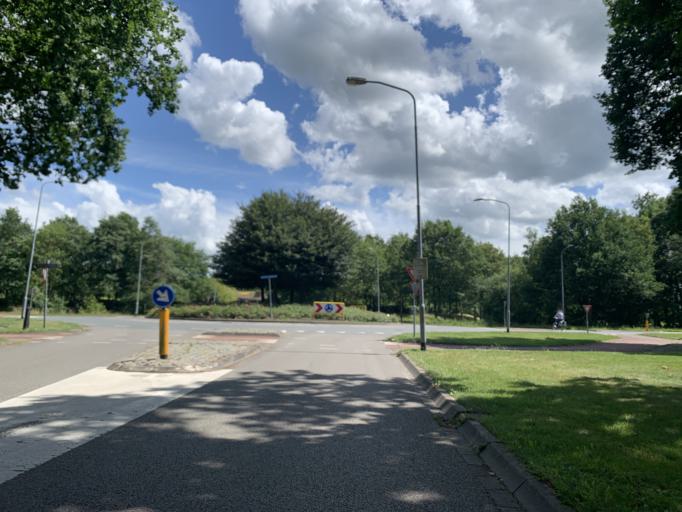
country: NL
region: Groningen
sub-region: Gemeente Haren
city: Haren
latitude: 53.1622
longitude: 6.6175
